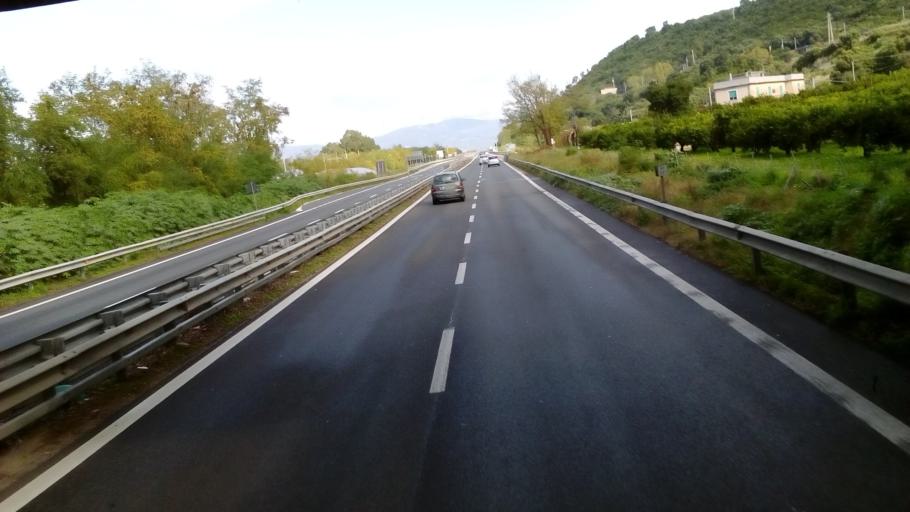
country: IT
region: Calabria
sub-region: Provincia di Vibo-Valentia
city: Pizzo
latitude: 38.7776
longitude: 16.2161
